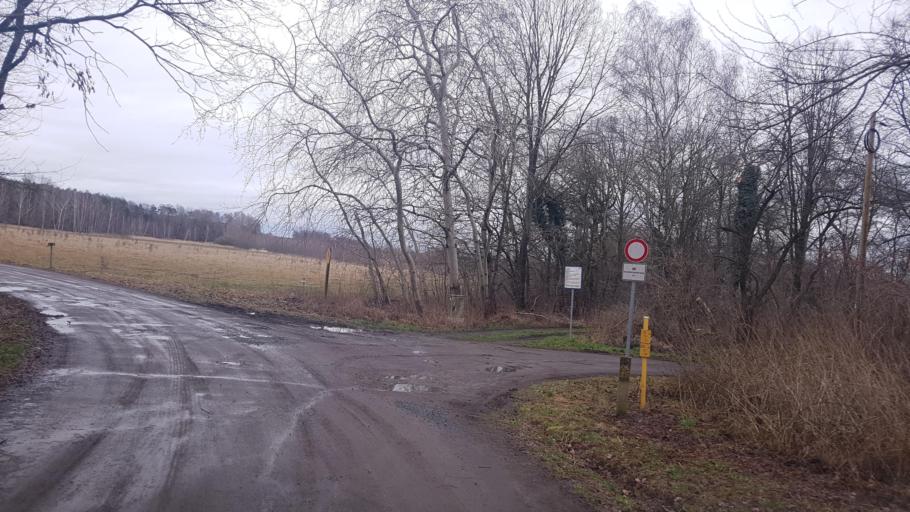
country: DE
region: Brandenburg
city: Elsterwerda
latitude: 51.4736
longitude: 13.5207
